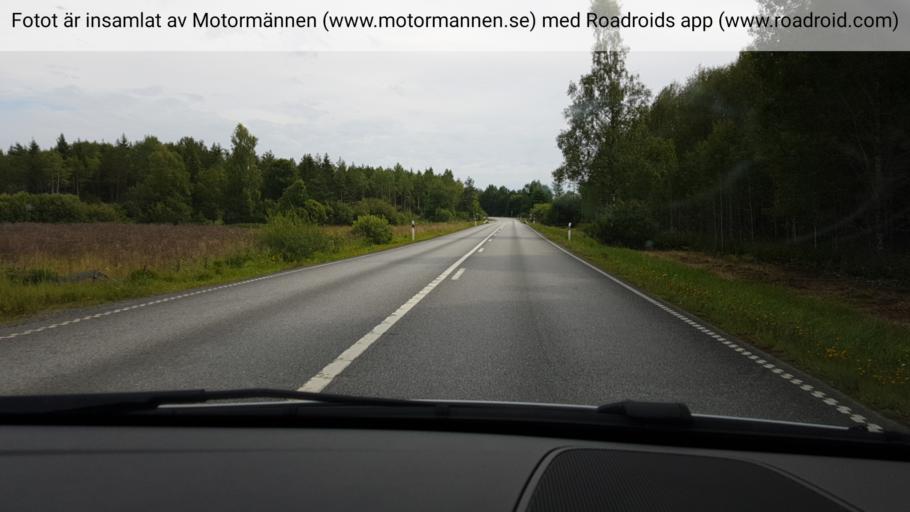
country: SE
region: Stockholm
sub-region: Norrtalje Kommun
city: Hallstavik
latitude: 60.0921
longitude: 18.4810
